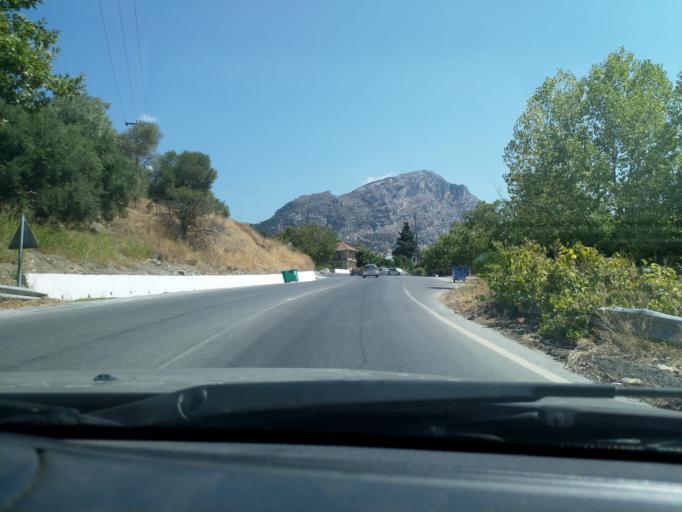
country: GR
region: Crete
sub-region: Nomos Rethymnis
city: Agia Foteini
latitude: 35.2208
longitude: 24.5182
